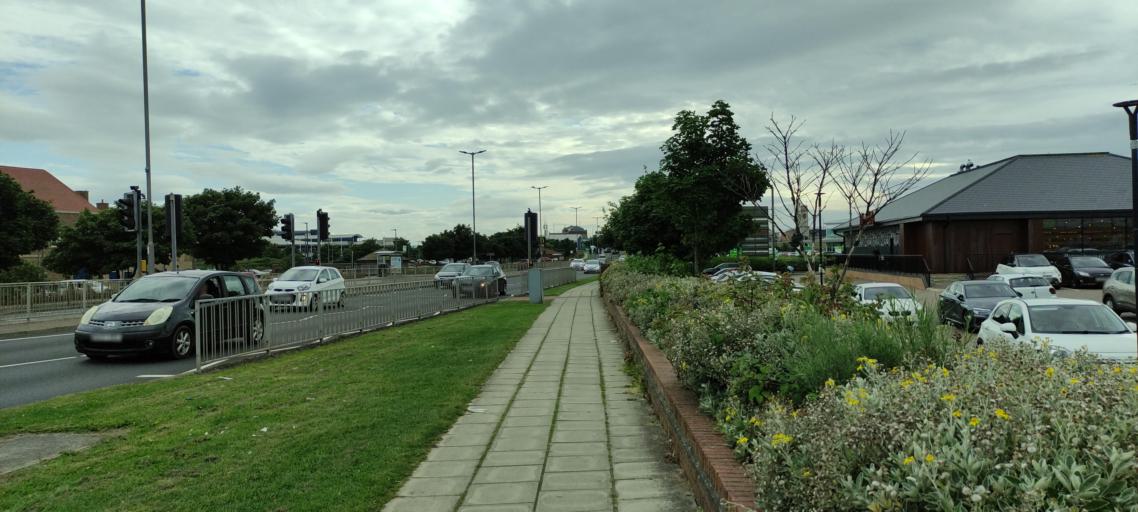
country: GB
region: England
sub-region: Hartlepool
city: Hartlepool
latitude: 54.6911
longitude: -1.2093
